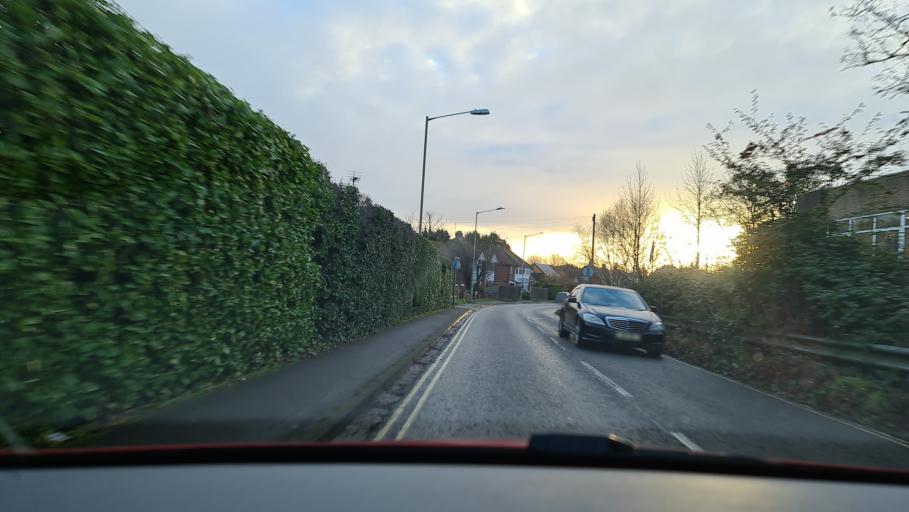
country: GB
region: England
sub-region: Oxfordshire
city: Thame
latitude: 51.7402
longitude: -0.9635
